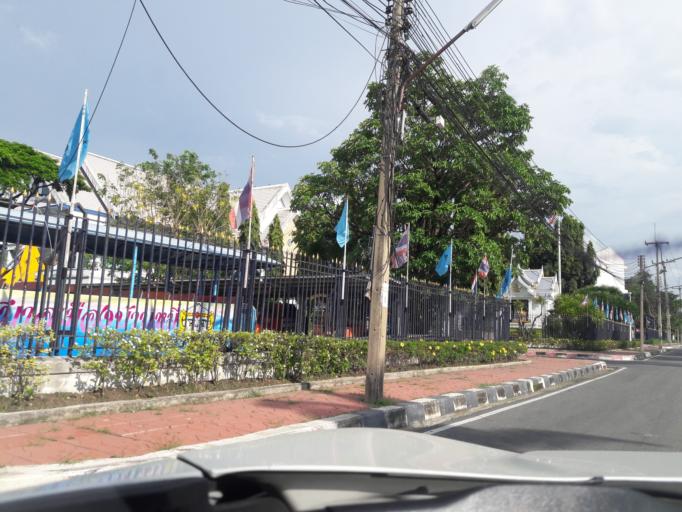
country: TH
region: Lop Buri
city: Ban Mi
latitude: 15.0461
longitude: 100.5351
